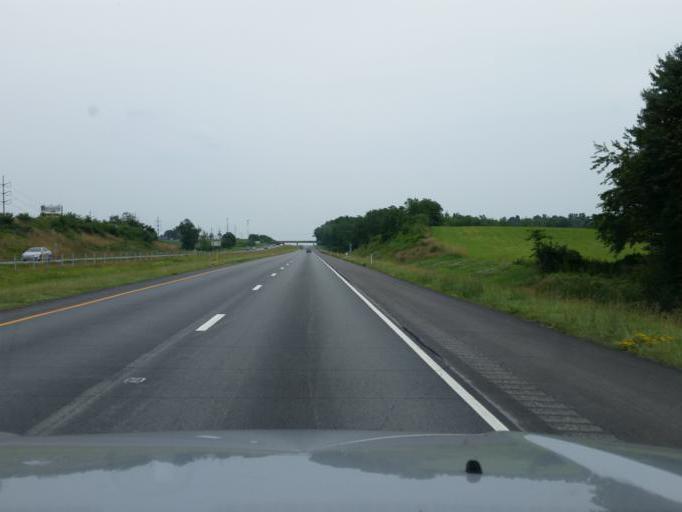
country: US
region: Pennsylvania
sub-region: Lancaster County
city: Elizabethtown
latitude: 40.1611
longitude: -76.5791
